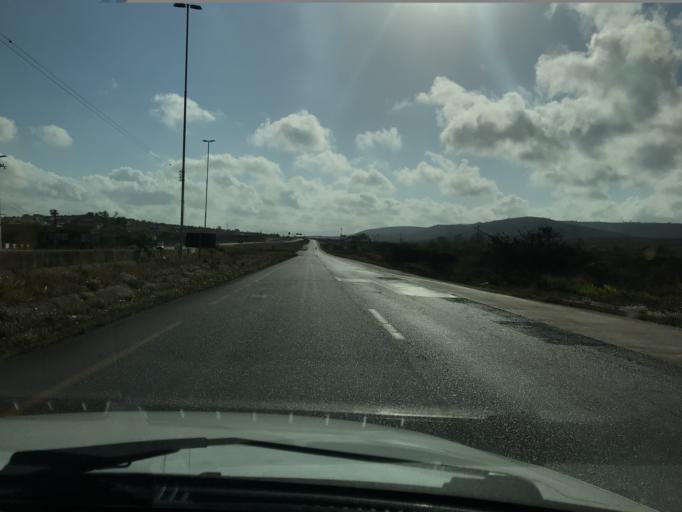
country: BR
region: Pernambuco
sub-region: Bezerros
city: Bezerros
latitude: -8.2360
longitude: -35.7272
